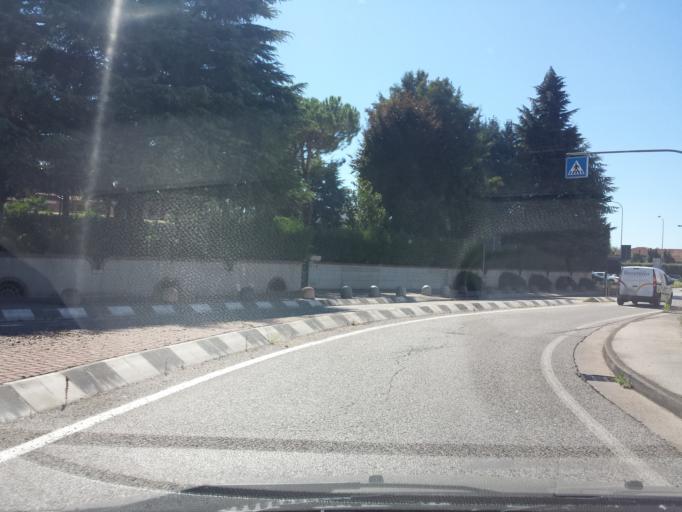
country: IT
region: Veneto
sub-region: Provincia di Vicenza
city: Dueville
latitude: 45.6237
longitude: 11.5693
